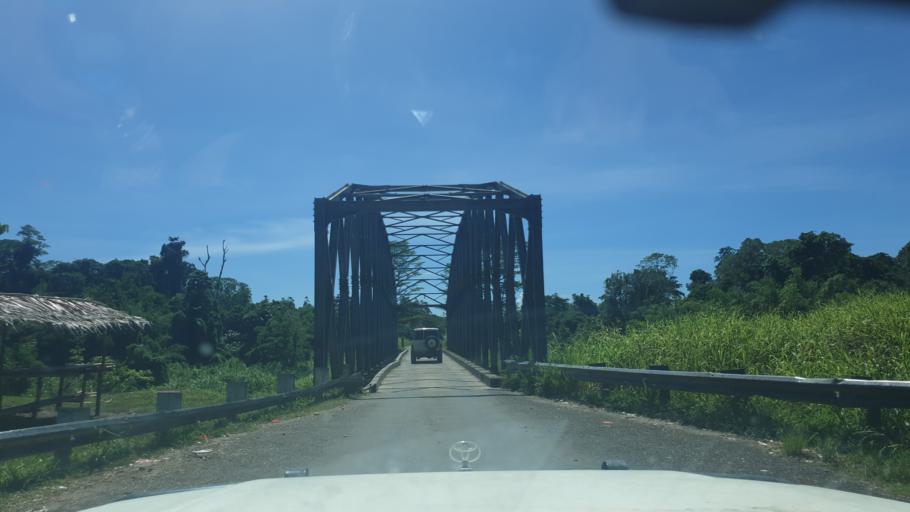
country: PG
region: Bougainville
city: Arawa
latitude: -5.8188
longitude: 155.1476
